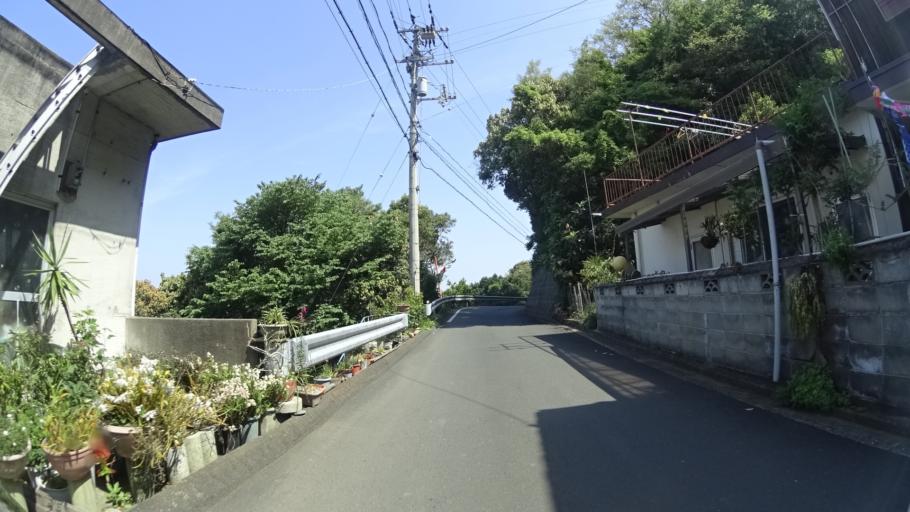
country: JP
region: Oita
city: Tsukumiura
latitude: 33.3528
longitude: 132.0304
